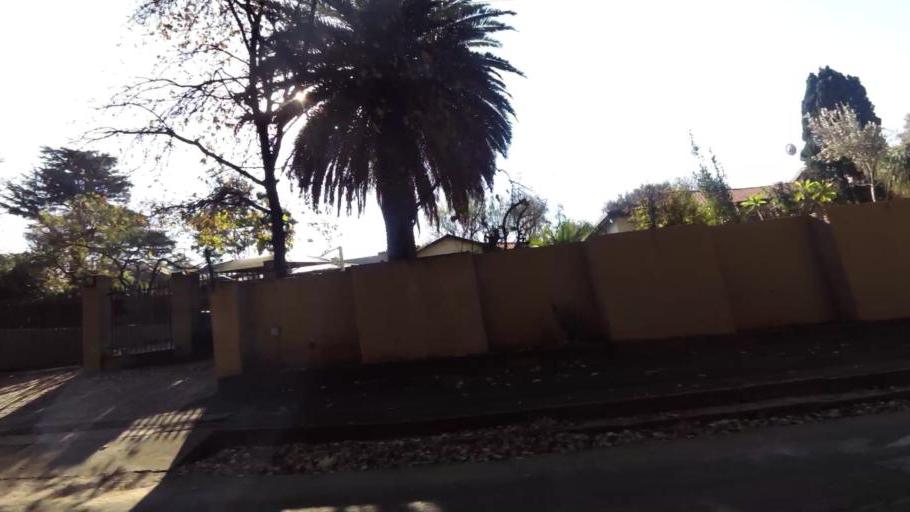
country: ZA
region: Gauteng
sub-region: City of Johannesburg Metropolitan Municipality
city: Johannesburg
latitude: -26.1804
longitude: 28.0112
